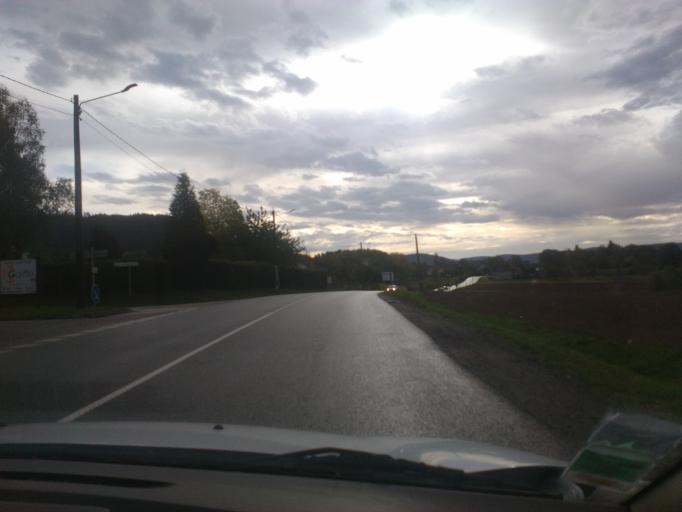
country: FR
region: Lorraine
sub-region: Departement des Vosges
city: Bruyeres
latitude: 48.1972
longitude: 6.7318
